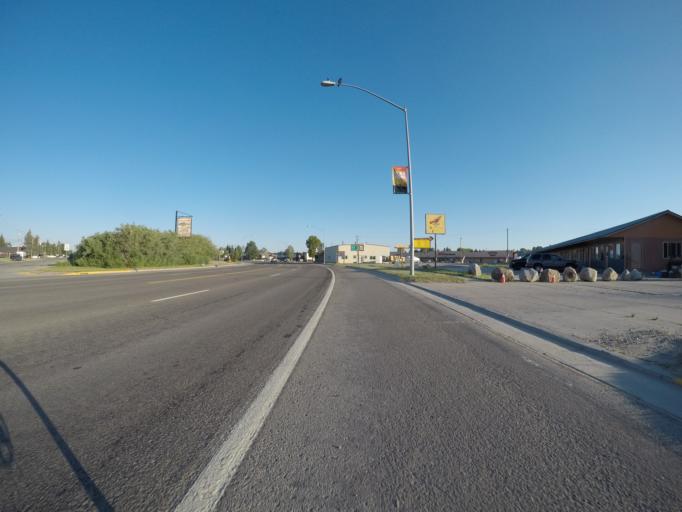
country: US
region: Wyoming
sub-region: Sublette County
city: Pinedale
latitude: 42.8657
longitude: -109.8549
